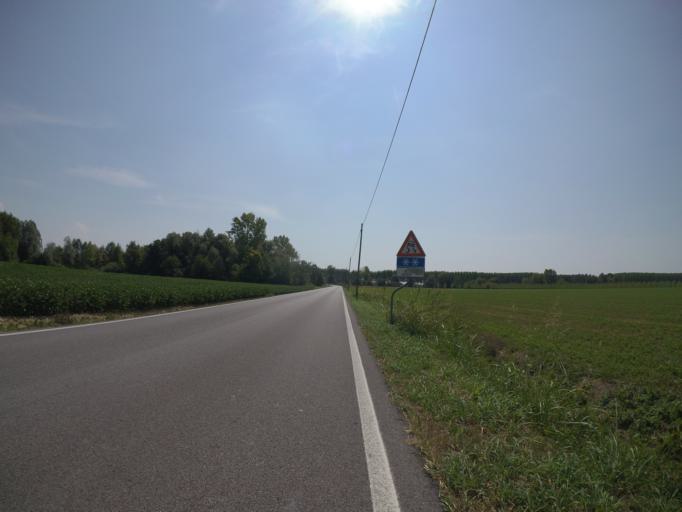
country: IT
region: Friuli Venezia Giulia
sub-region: Provincia di Udine
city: Pocenia
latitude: 45.8485
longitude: 13.0931
